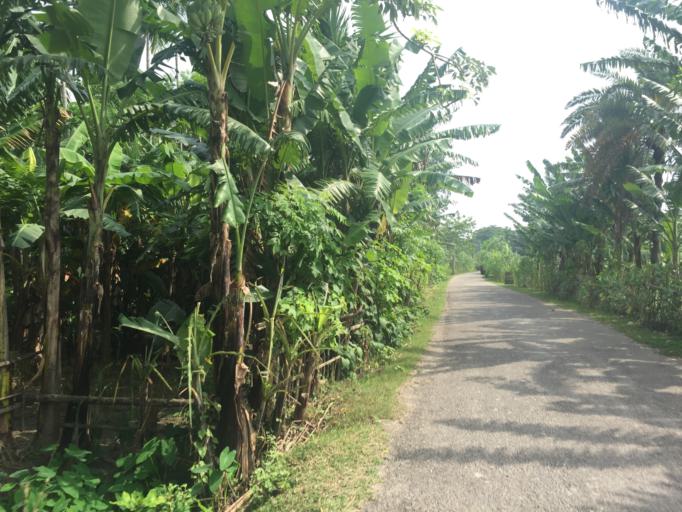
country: BD
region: Barisal
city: Mathba
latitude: 22.2577
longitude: 89.9108
